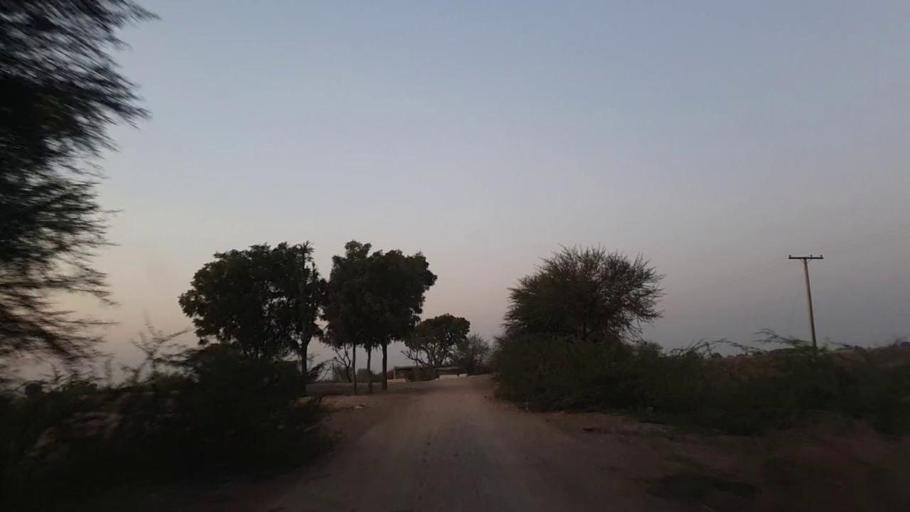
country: PK
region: Sindh
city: Naukot
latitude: 24.8917
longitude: 69.3839
